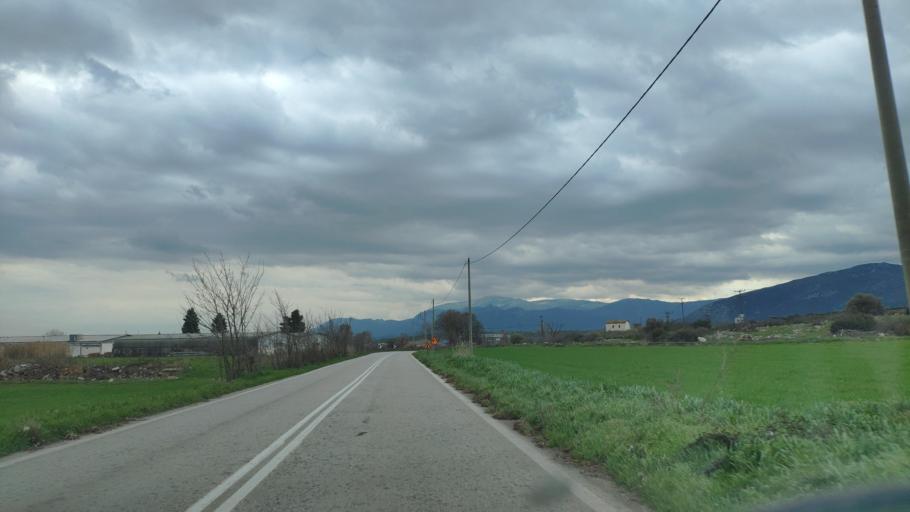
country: GR
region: Central Greece
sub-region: Nomos Voiotias
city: Livadeia
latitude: 38.4707
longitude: 22.9179
